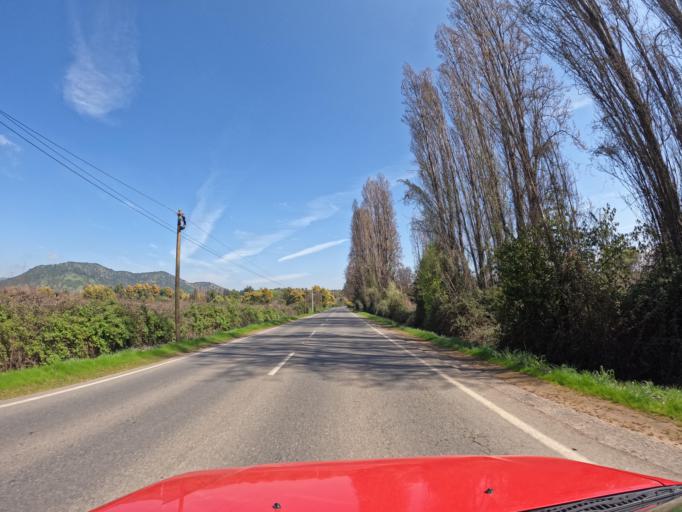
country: CL
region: Maule
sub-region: Provincia de Talca
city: San Clemente
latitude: -35.4874
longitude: -71.2924
